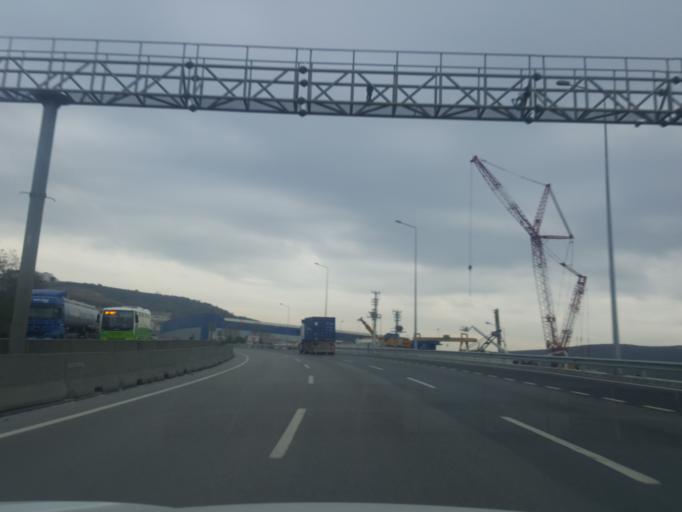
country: TR
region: Kocaeli
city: Tavsanli
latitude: 40.7946
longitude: 29.5268
